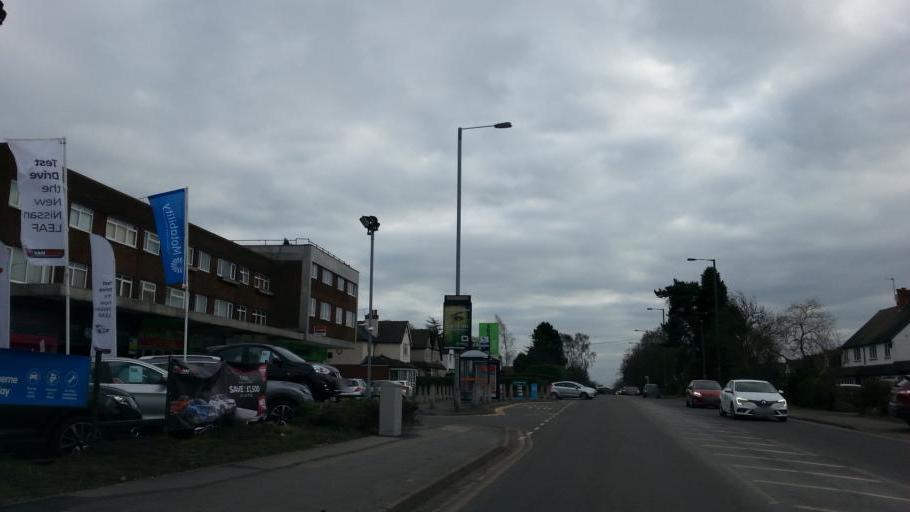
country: GB
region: England
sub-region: Walsall
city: Streetly
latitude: 52.5772
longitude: -1.8841
